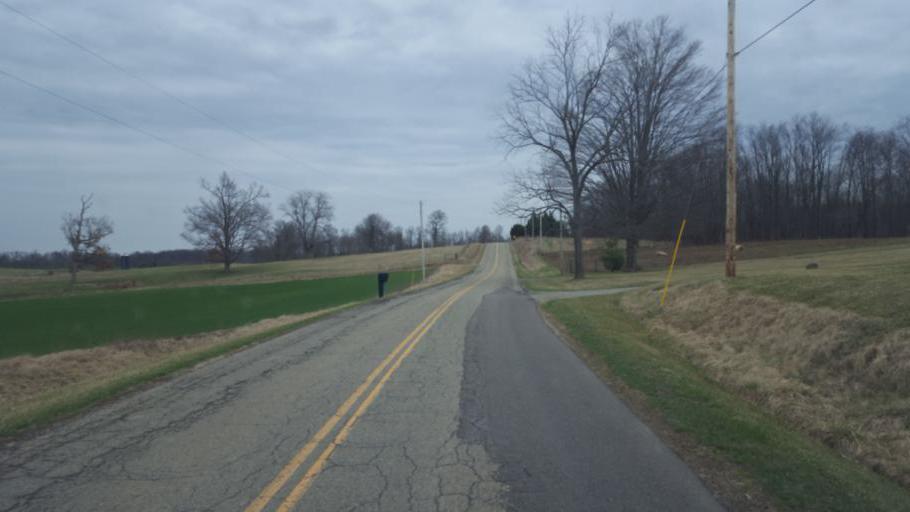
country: US
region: Ohio
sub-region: Knox County
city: Fredericktown
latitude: 40.5154
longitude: -82.4139
